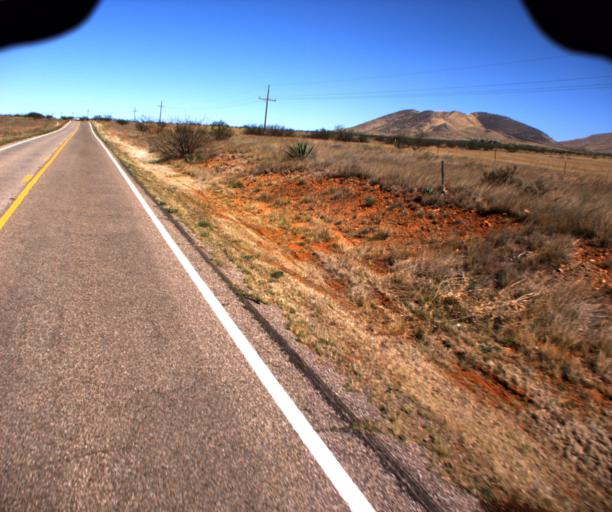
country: US
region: Arizona
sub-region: Cochise County
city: Huachuca City
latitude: 31.7073
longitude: -110.4427
